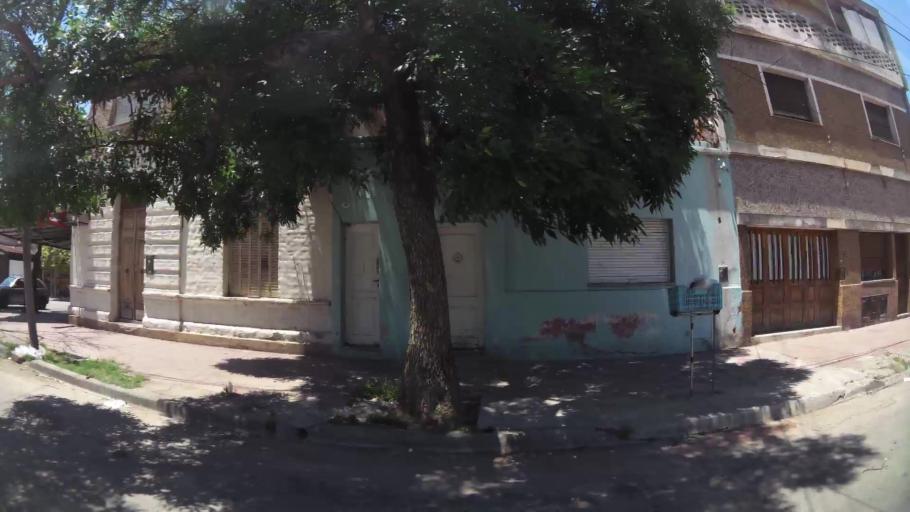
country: AR
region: Cordoba
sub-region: Departamento de Capital
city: Cordoba
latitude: -31.4029
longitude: -64.2156
